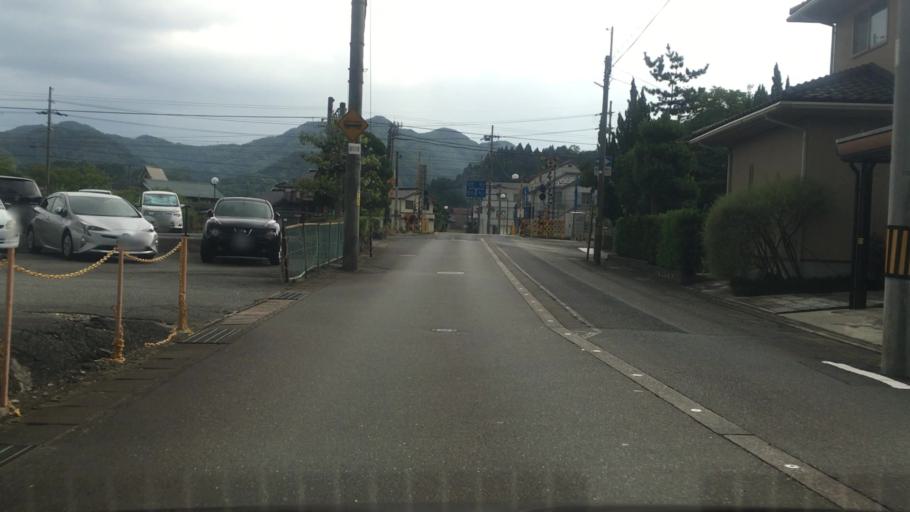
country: JP
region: Hyogo
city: Toyooka
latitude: 35.4719
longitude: 134.7769
